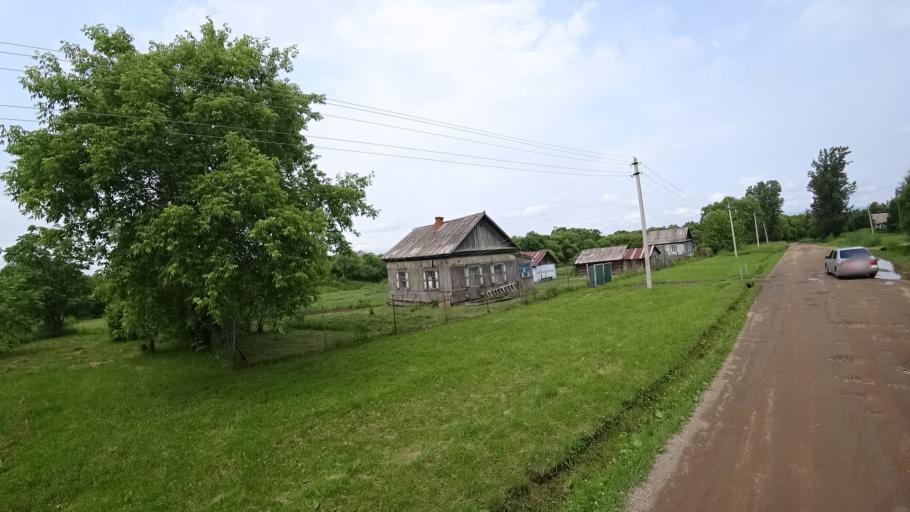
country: RU
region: Primorskiy
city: Novosysoyevka
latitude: 44.2502
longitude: 133.3765
